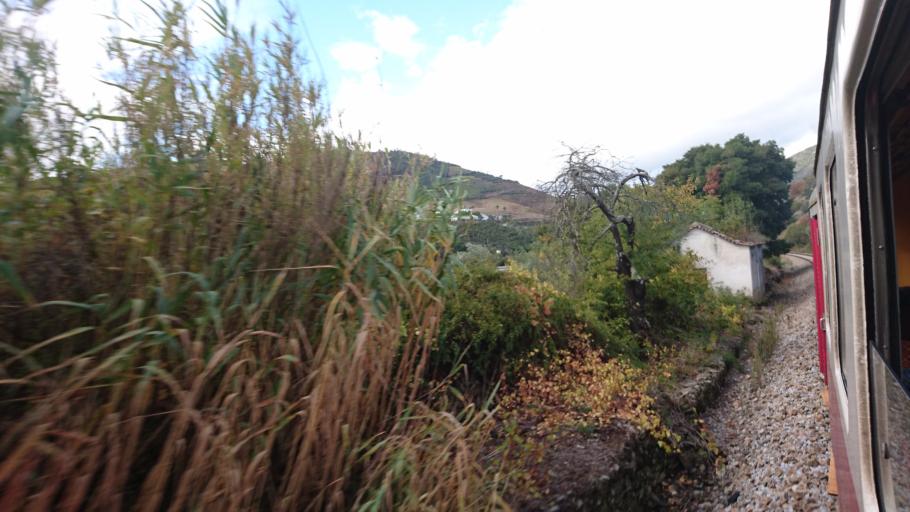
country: PT
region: Vila Real
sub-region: Sabrosa
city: Vilela
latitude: 41.1602
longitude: -7.6385
